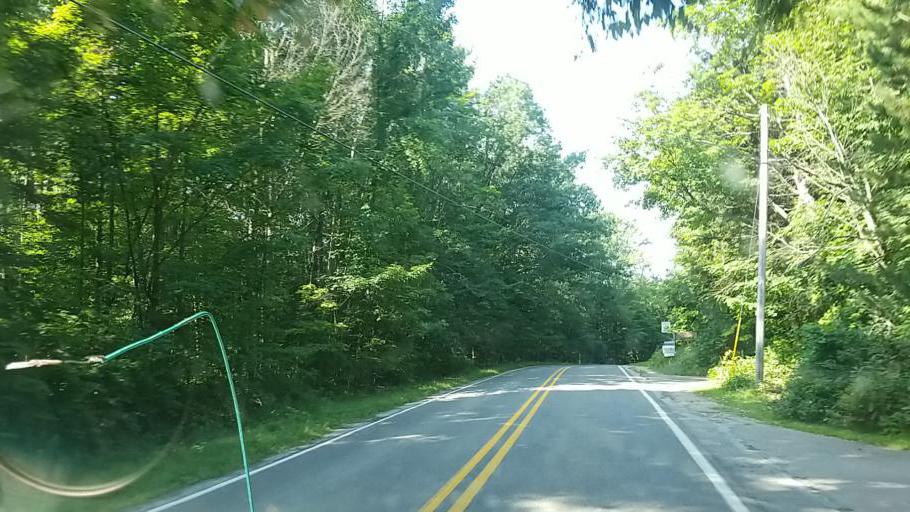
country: US
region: Michigan
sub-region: Muskegon County
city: Whitehall
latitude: 43.3751
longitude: -86.3715
